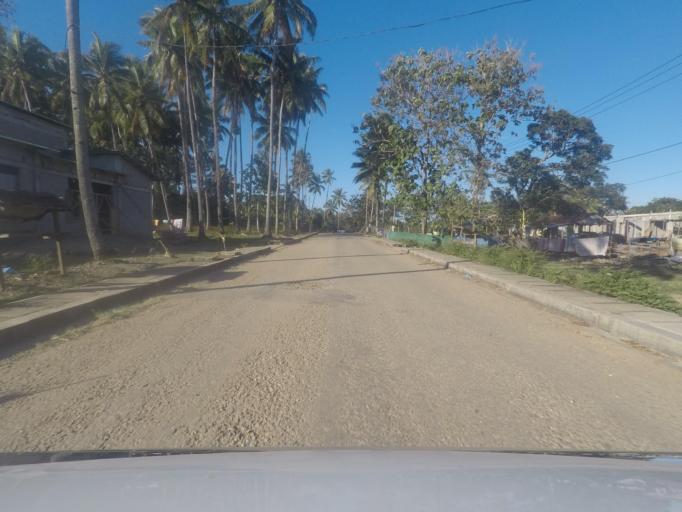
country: TL
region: Lautem
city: Lospalos
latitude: -8.4004
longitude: 127.1837
